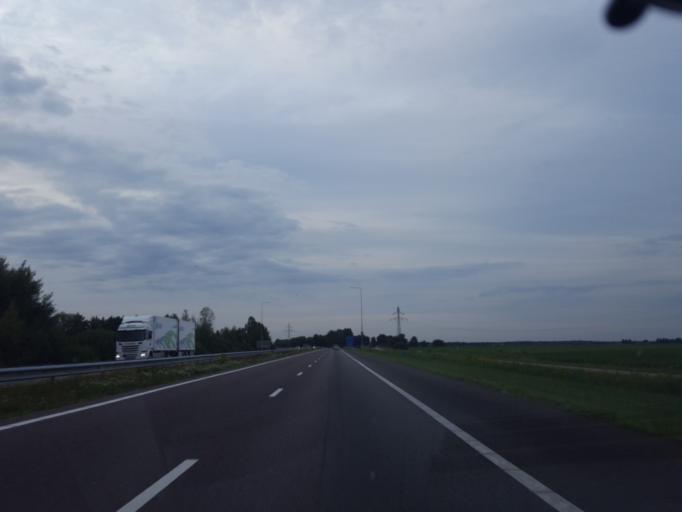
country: NL
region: Drenthe
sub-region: Gemeente Meppel
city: Meppel
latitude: 52.7132
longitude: 6.2055
